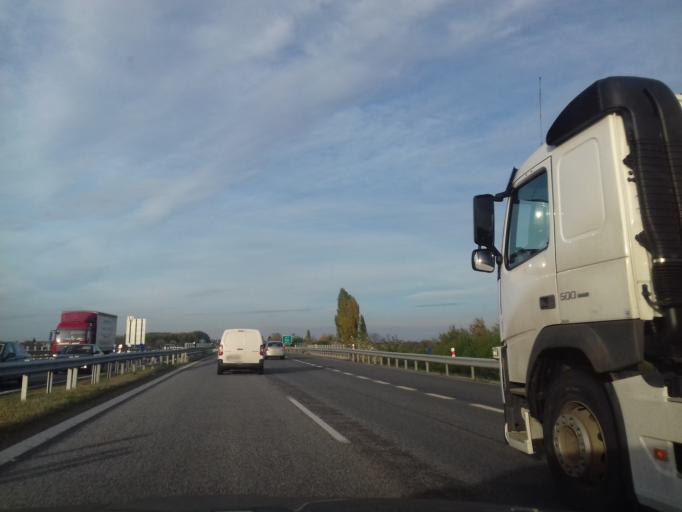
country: SK
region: Trnavsky
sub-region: Okres Galanta
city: Galanta
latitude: 48.2652
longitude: 17.8137
